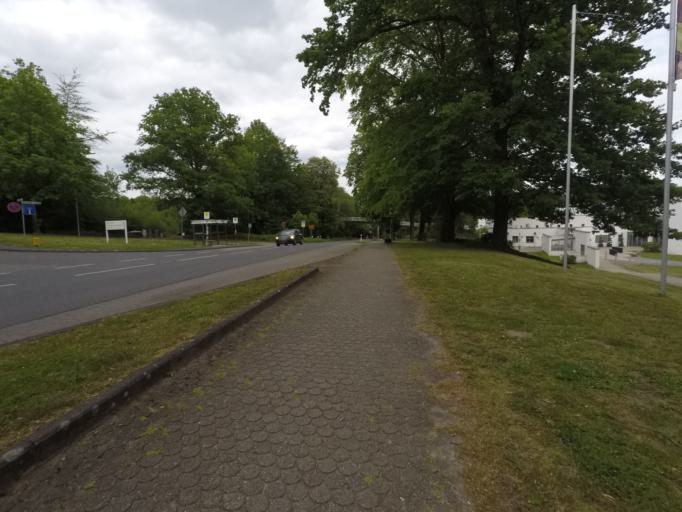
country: DE
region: North Rhine-Westphalia
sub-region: Regierungsbezirk Detmold
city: Bad Salzuflen
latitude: 52.0959
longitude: 8.7512
